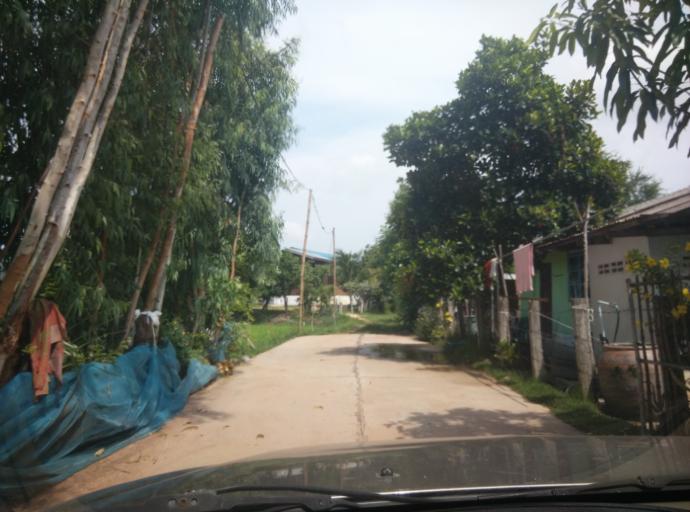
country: TH
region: Sisaket
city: Huai Thap Than
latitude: 14.9830
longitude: 104.0698
